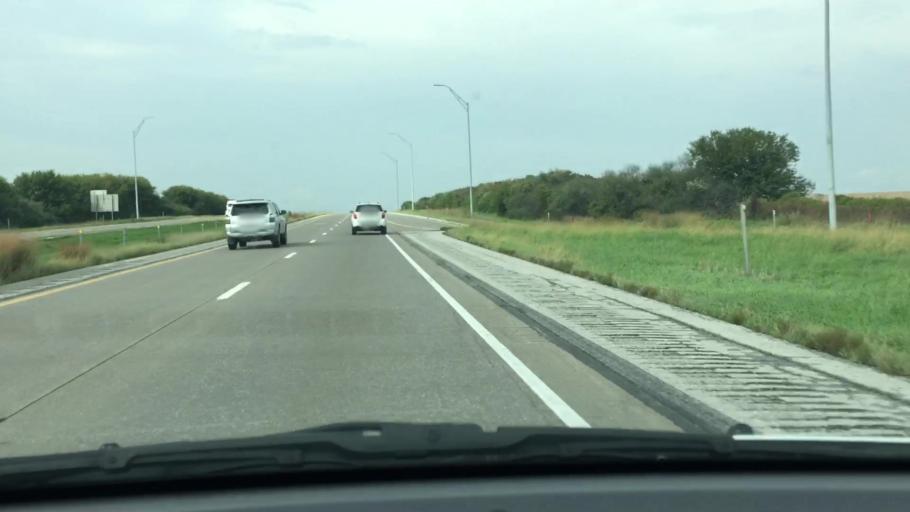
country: US
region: Iowa
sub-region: Cedar County
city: Durant
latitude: 41.6332
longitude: -90.8638
